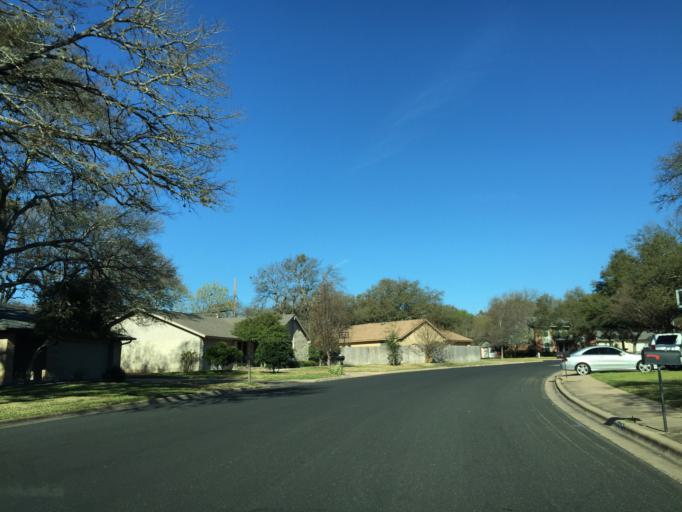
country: US
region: Texas
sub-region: Williamson County
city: Jollyville
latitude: 30.4032
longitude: -97.7359
